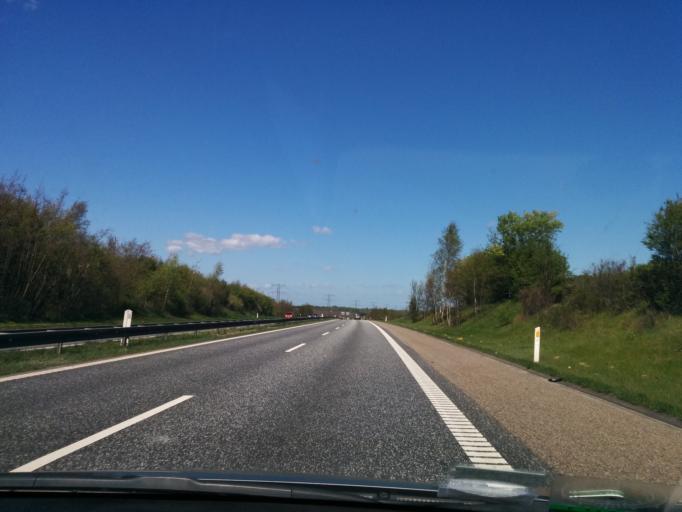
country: DK
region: Central Jutland
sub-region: Arhus Kommune
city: Trige
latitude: 56.2369
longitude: 10.1253
